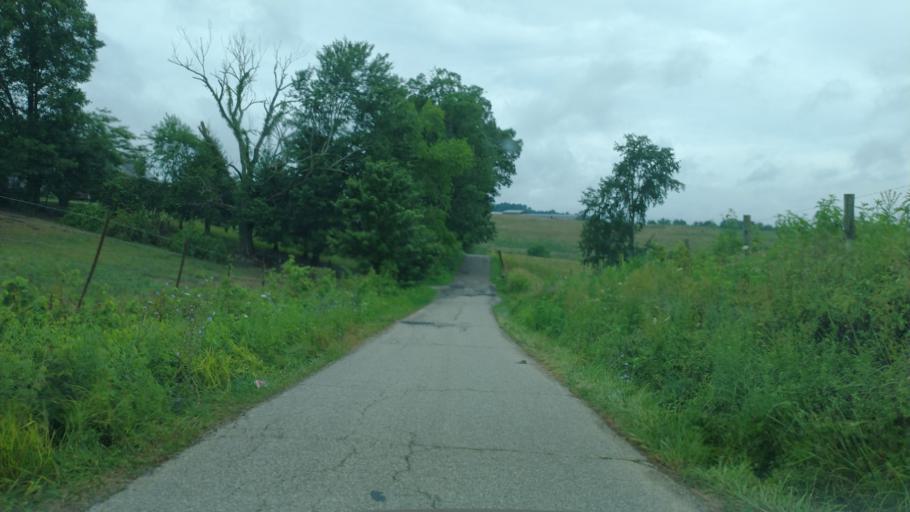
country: US
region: West Virginia
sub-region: Mason County
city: New Haven
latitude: 38.9261
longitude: -81.9630
